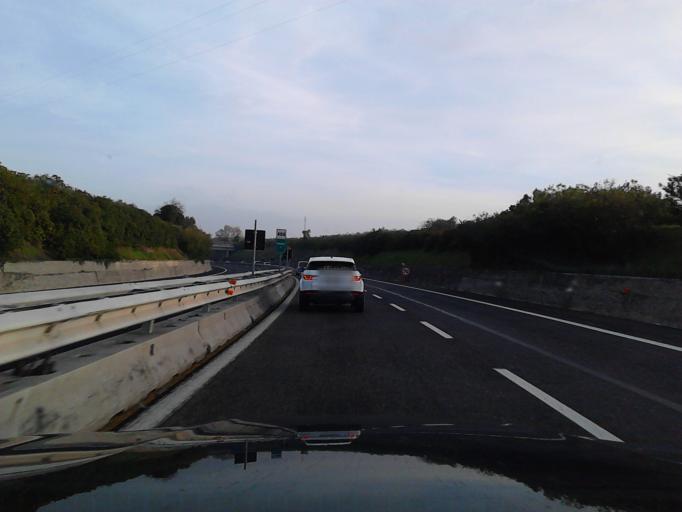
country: IT
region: Abruzzo
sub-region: Provincia di Chieti
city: Ortona
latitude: 42.3171
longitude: 14.4011
